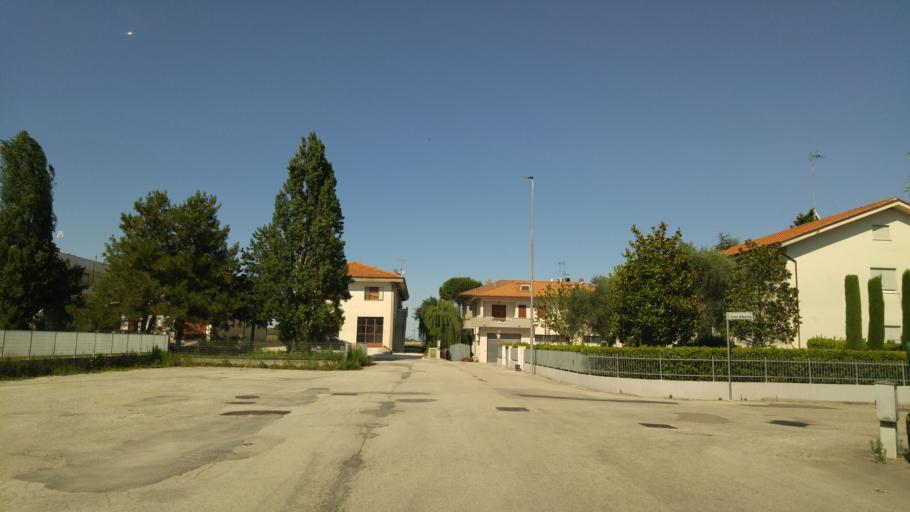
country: IT
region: The Marches
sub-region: Provincia di Pesaro e Urbino
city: Mondolfo
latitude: 43.7401
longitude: 13.1058
